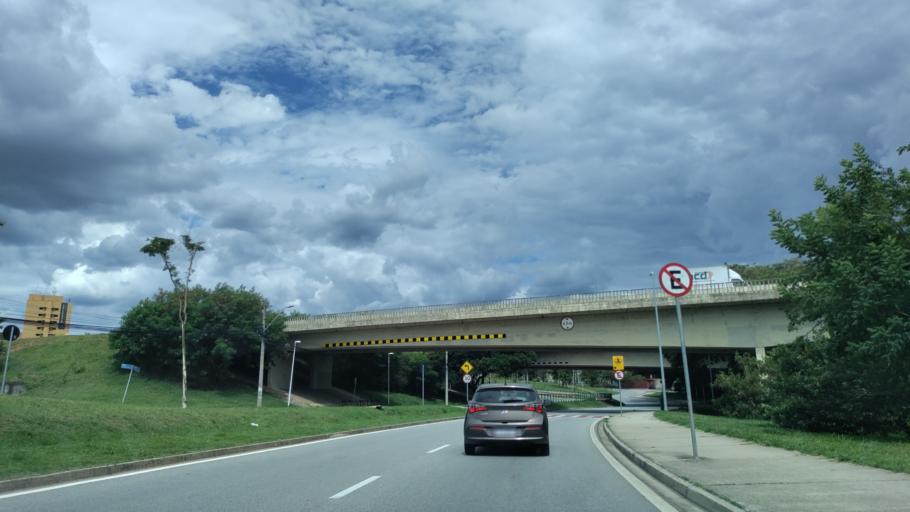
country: BR
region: Sao Paulo
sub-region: Sorocaba
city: Sorocaba
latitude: -23.4774
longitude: -47.4398
